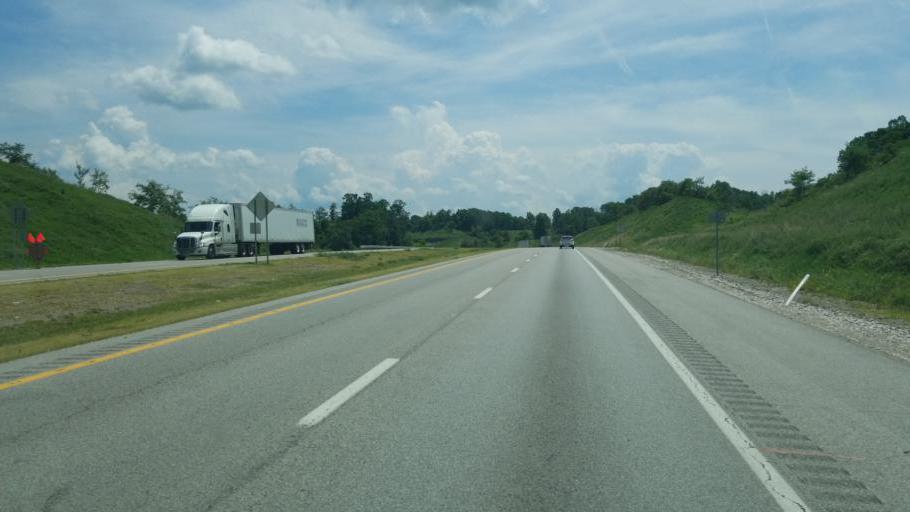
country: US
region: West Virginia
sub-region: Mason County
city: Point Pleasant
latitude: 38.7935
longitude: -82.0960
